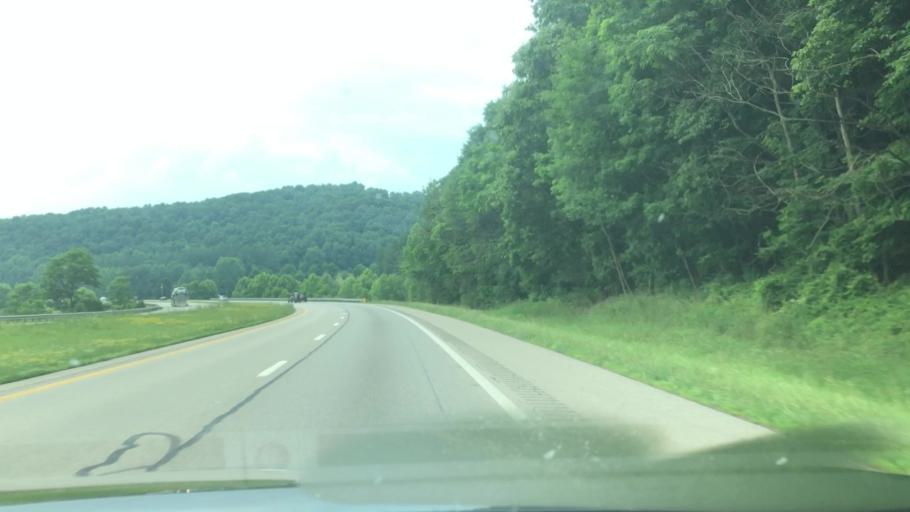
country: US
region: Ohio
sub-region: Jackson County
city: Jackson
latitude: 39.1600
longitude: -82.7333
